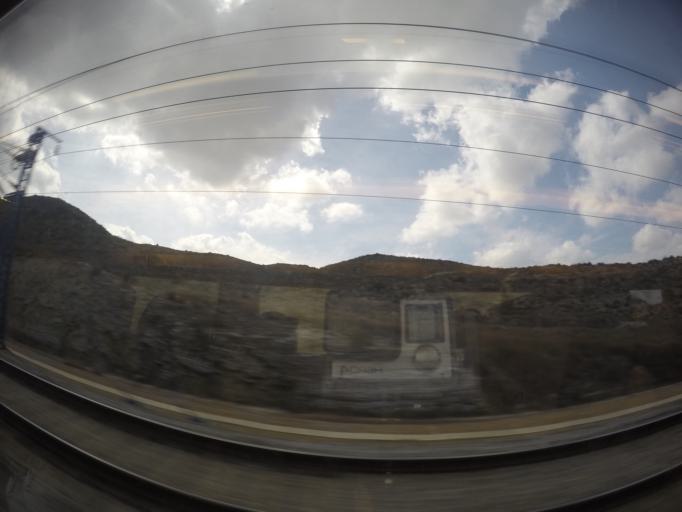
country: ES
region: Aragon
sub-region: Provincia de Zaragoza
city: Fuentes de Ebro
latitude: 41.4975
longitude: -0.6498
